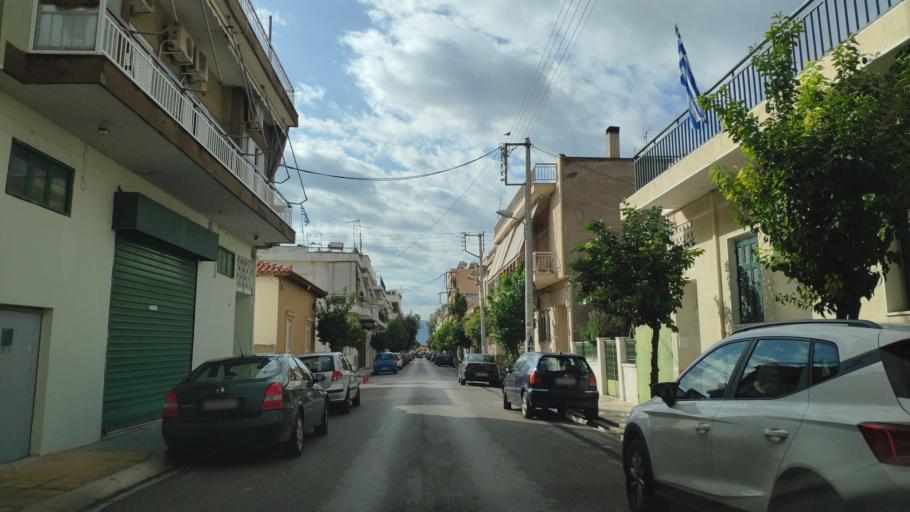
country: GR
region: Attica
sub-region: Nomarchia Dytikis Attikis
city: Elefsina
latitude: 38.0385
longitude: 23.5400
